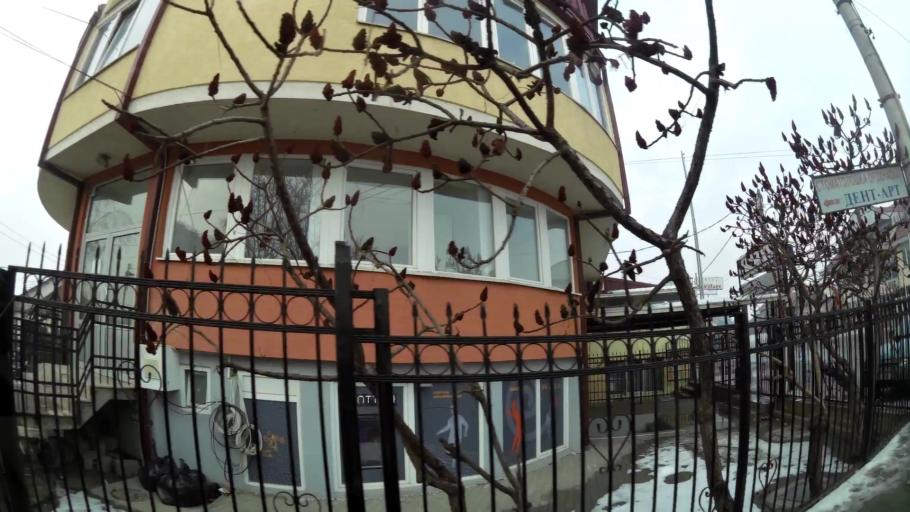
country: MK
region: Ilinden
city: Jurumleri
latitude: 41.9800
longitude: 21.5283
